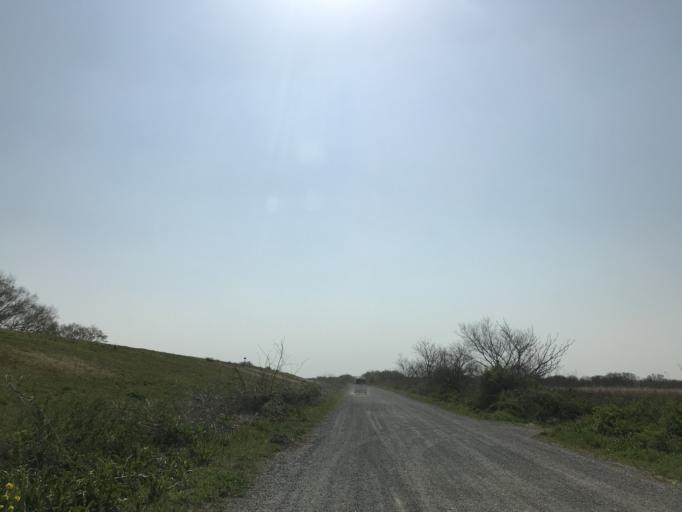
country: JP
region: Ibaraki
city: Moriya
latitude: 35.9192
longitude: 139.9849
